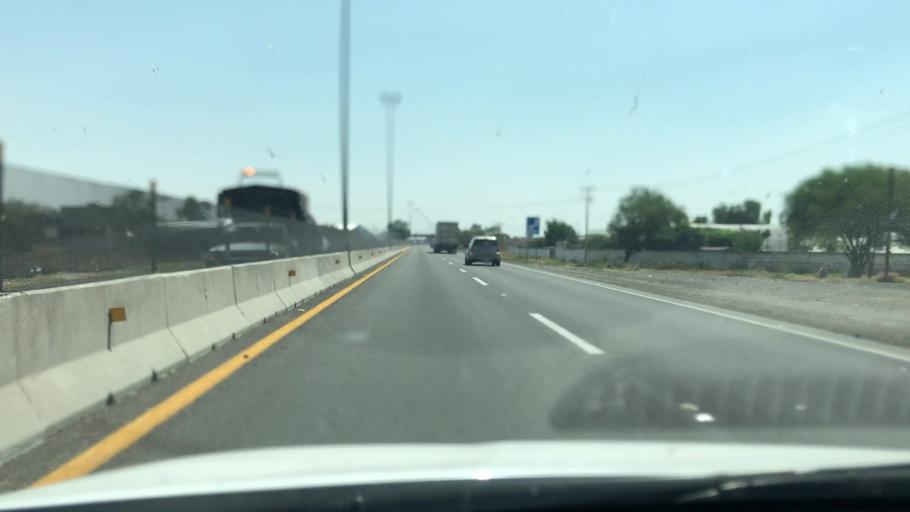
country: MX
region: Guanajuato
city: Abasolo
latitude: 20.4568
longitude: -101.5368
